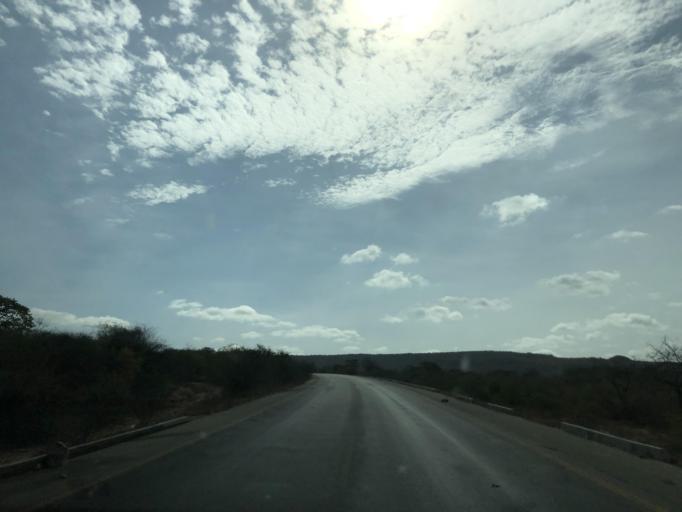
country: AO
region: Benguela
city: Benguela
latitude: -12.9799
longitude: 13.6225
